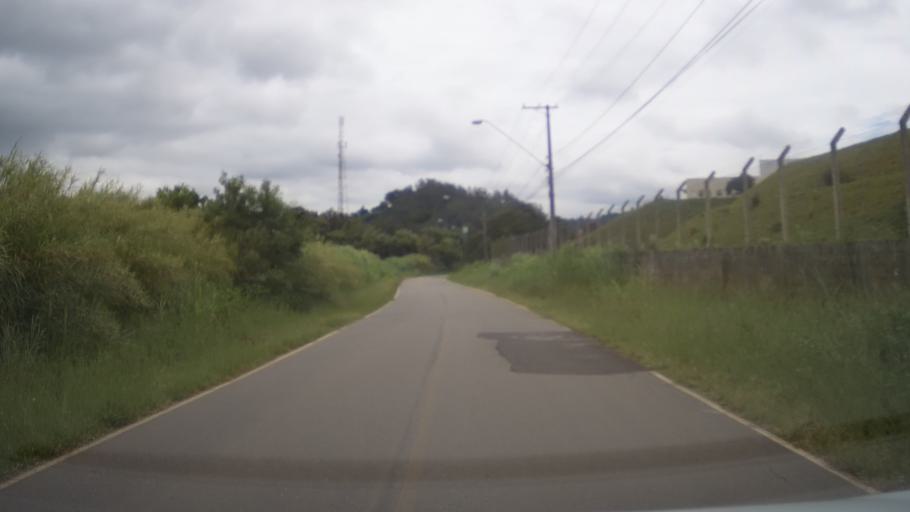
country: BR
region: Sao Paulo
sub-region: Vinhedo
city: Vinhedo
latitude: -23.0619
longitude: -47.0368
